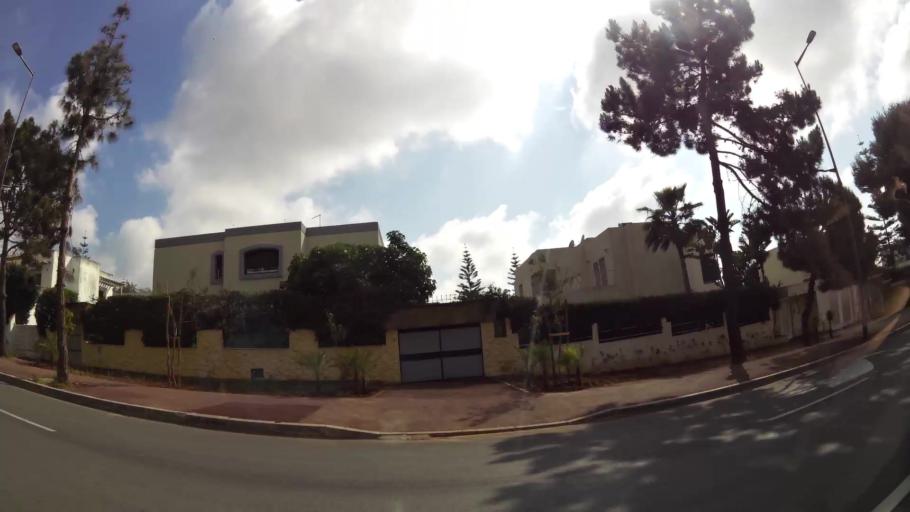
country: MA
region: Rabat-Sale-Zemmour-Zaer
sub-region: Skhirate-Temara
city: Temara
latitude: 33.9585
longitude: -6.8612
